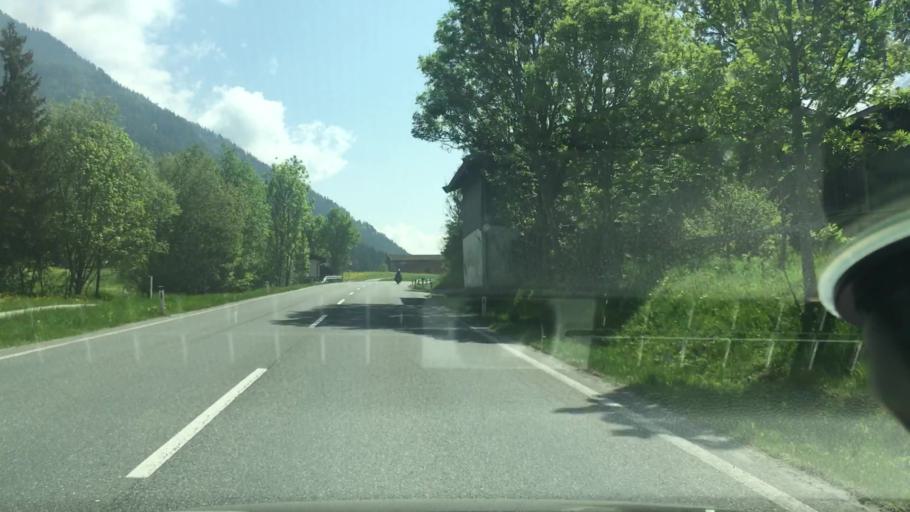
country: AT
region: Tyrol
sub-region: Politischer Bezirk Kitzbuhel
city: Waidring
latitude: 47.5923
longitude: 12.5457
